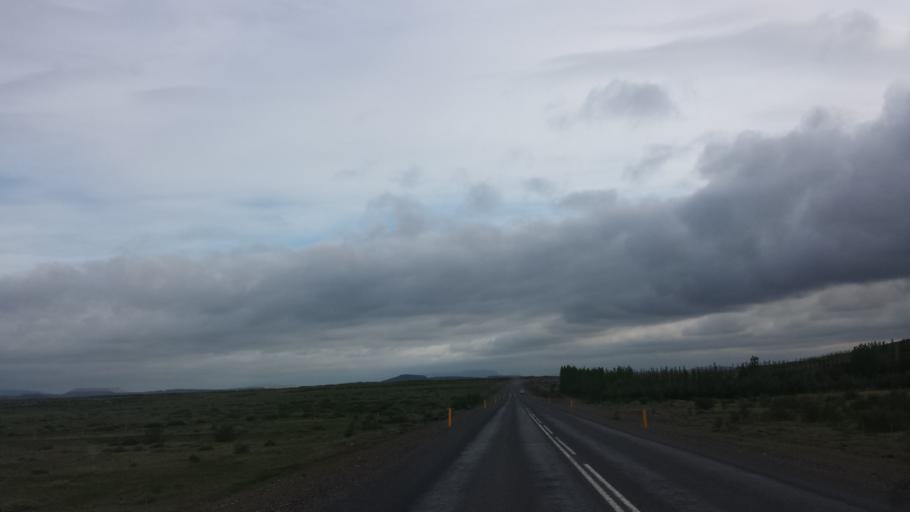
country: IS
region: South
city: Selfoss
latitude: 64.2837
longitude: -20.3422
